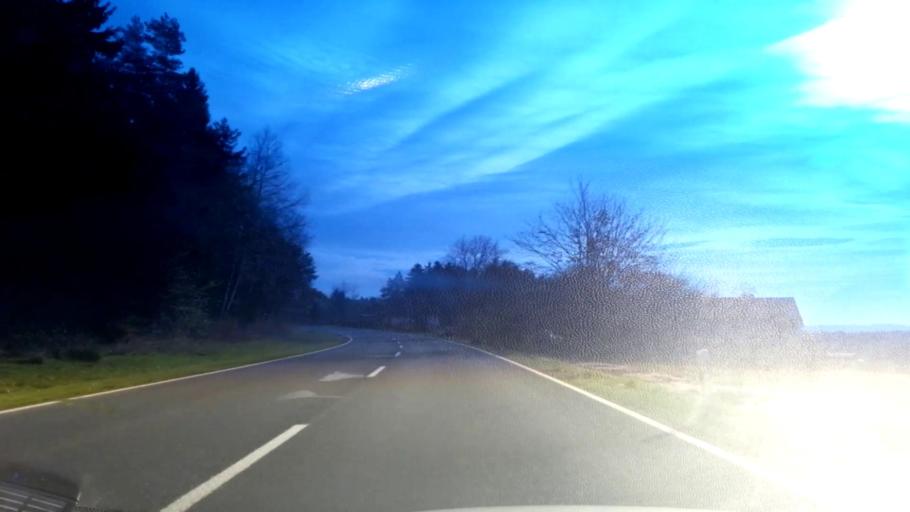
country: DE
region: Bavaria
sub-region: Upper Palatinate
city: Immenreuth
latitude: 49.9107
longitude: 11.8504
